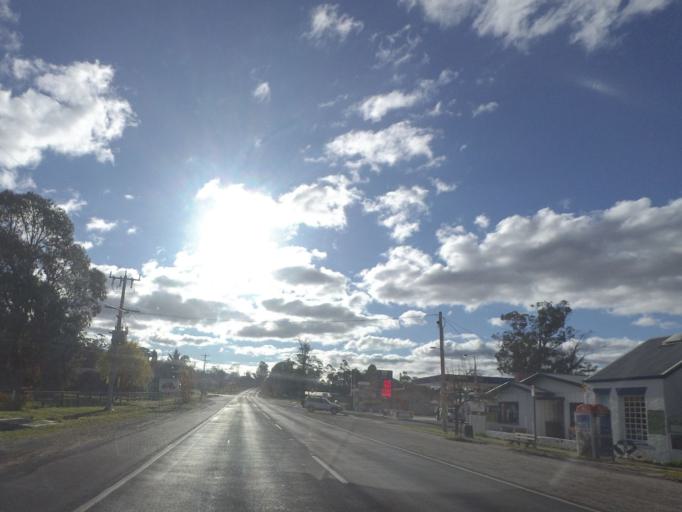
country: AU
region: Victoria
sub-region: Mount Alexander
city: Castlemaine
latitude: -37.1390
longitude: 144.3487
